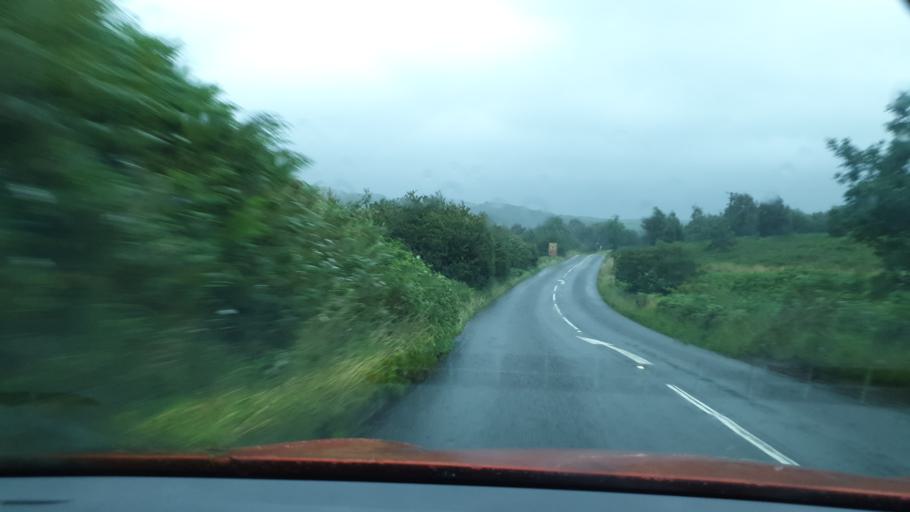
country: GB
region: England
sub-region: Cumbria
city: Ulverston
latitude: 54.2593
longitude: -3.0977
